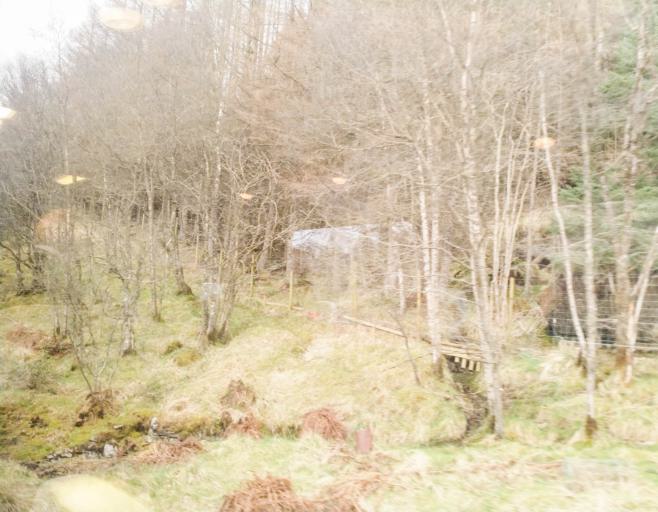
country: GB
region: Scotland
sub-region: Argyll and Bute
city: Garelochhead
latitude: 56.4356
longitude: -4.7045
